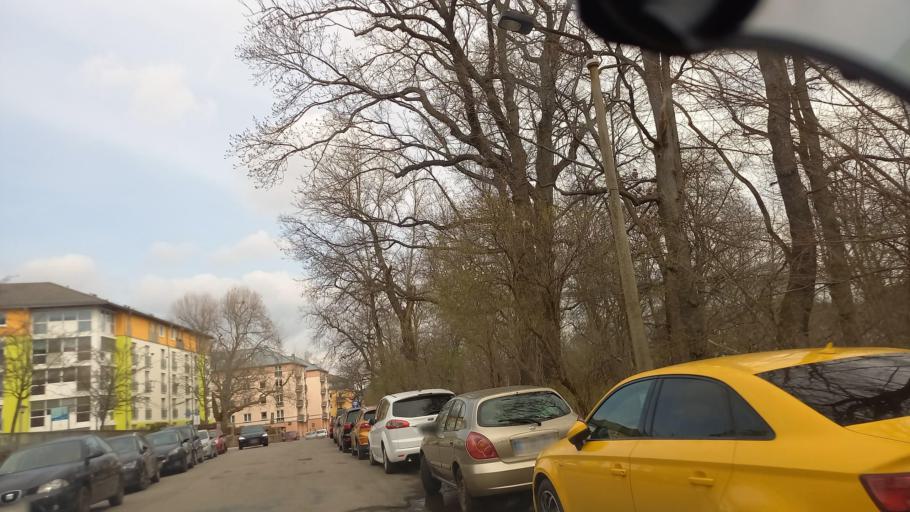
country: DE
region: Saxony
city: Zwickau
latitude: 50.7142
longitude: 12.4868
